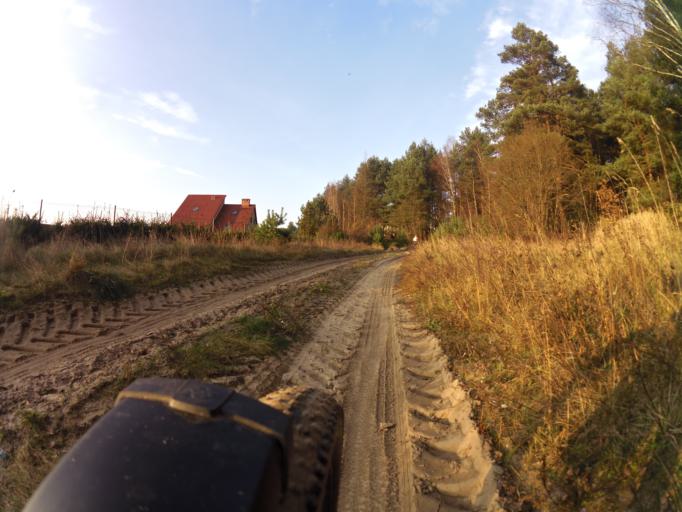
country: PL
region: West Pomeranian Voivodeship
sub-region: Powiat koszalinski
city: Polanow
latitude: 54.1265
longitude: 16.6890
